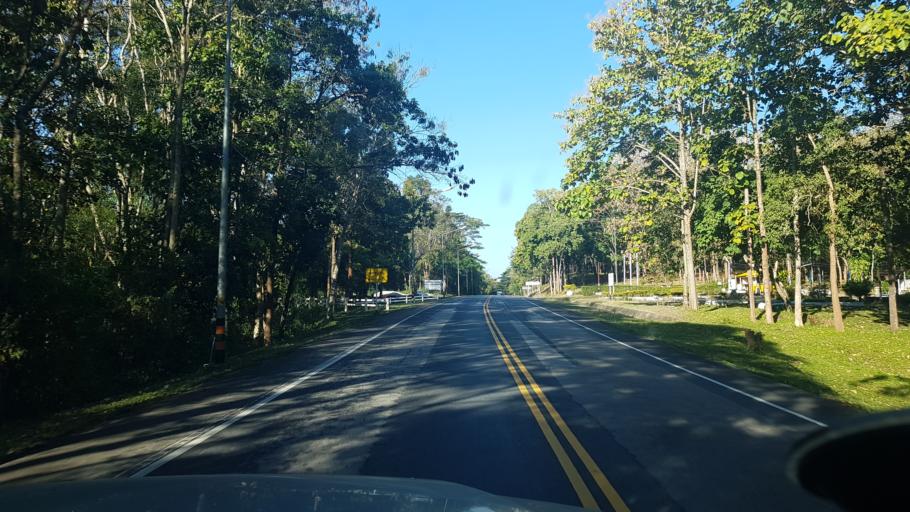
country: TH
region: Phetchabun
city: Lom Sak
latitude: 16.7359
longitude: 101.4342
